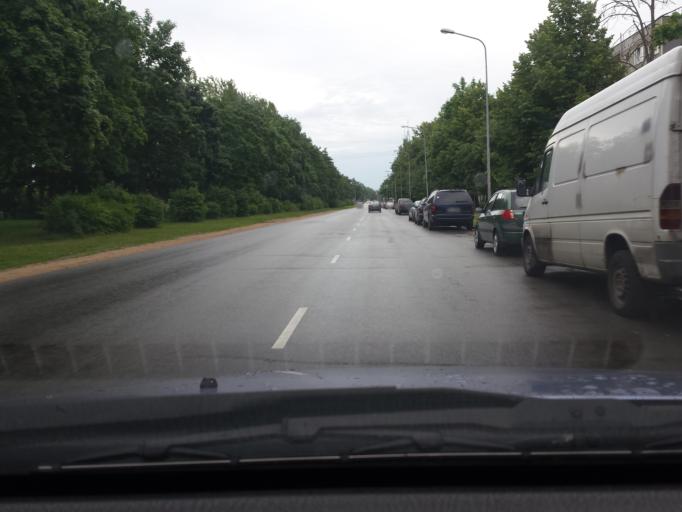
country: LV
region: Kekava
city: Kekava
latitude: 56.9069
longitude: 24.2056
